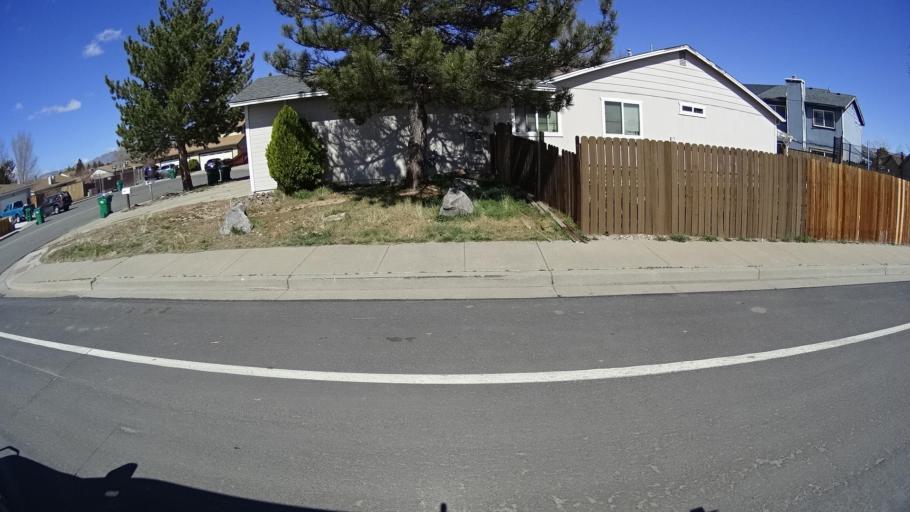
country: US
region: Nevada
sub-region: Washoe County
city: Lemmon Valley
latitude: 39.6424
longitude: -119.8784
